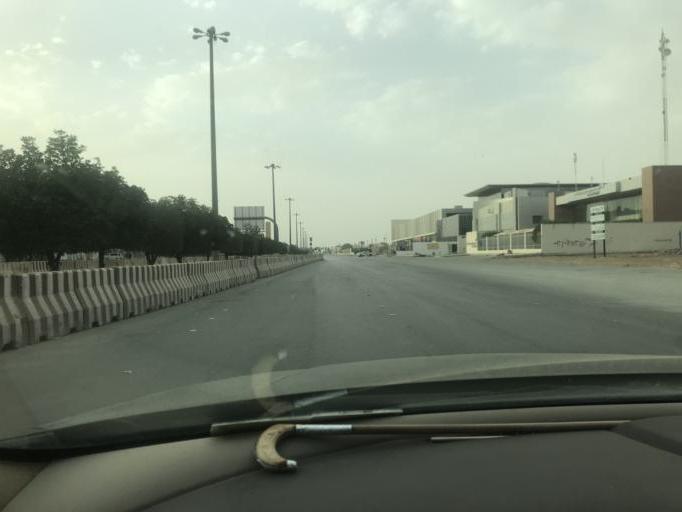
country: SA
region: Ar Riyad
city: Riyadh
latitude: 24.7874
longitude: 46.6597
